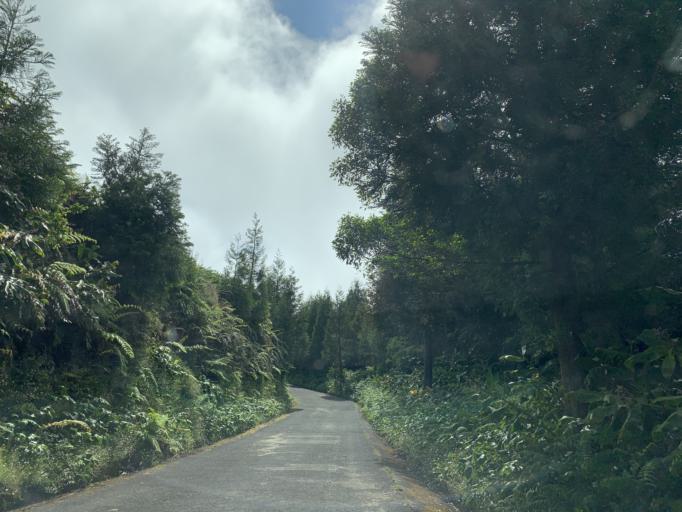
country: PT
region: Azores
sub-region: Ponta Delgada
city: Arrifes
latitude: 37.8497
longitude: -25.7380
